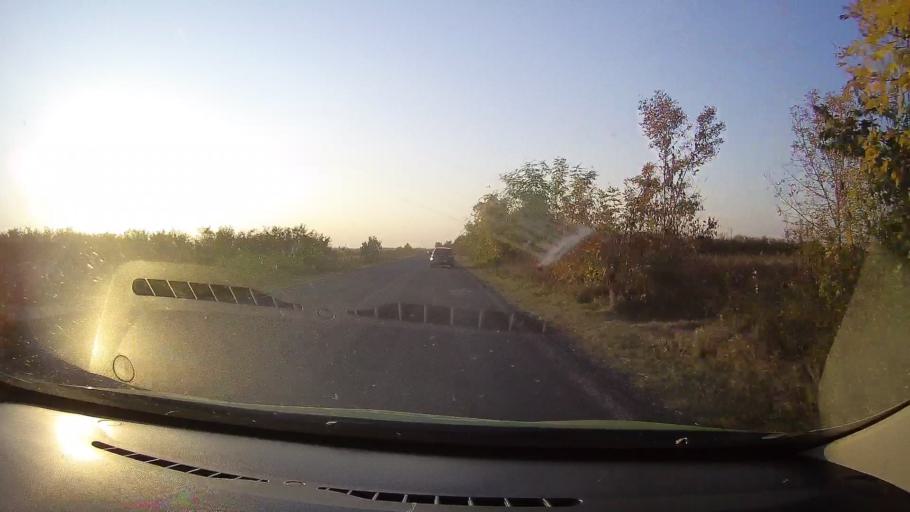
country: RO
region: Arad
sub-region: Comuna Bocsig
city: Bocsig
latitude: 46.4188
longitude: 21.9777
